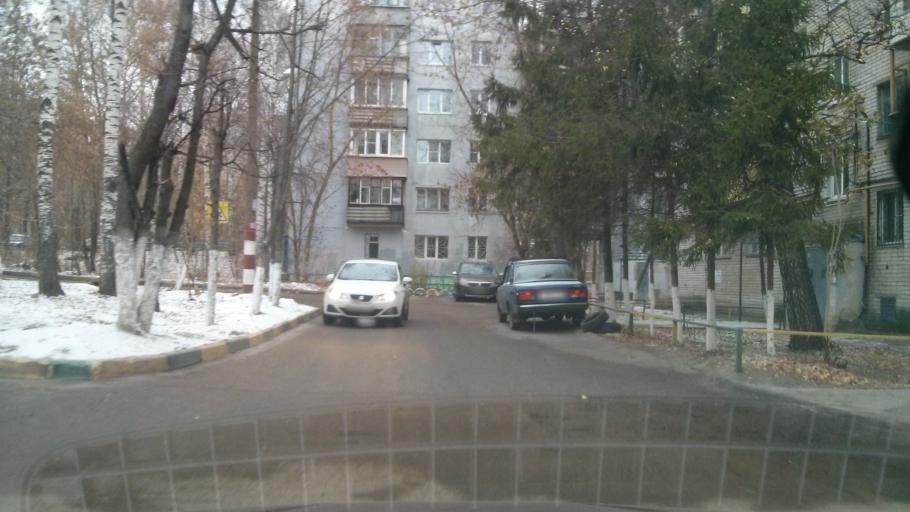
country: RU
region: Nizjnij Novgorod
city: Afonino
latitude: 56.2926
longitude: 44.0534
